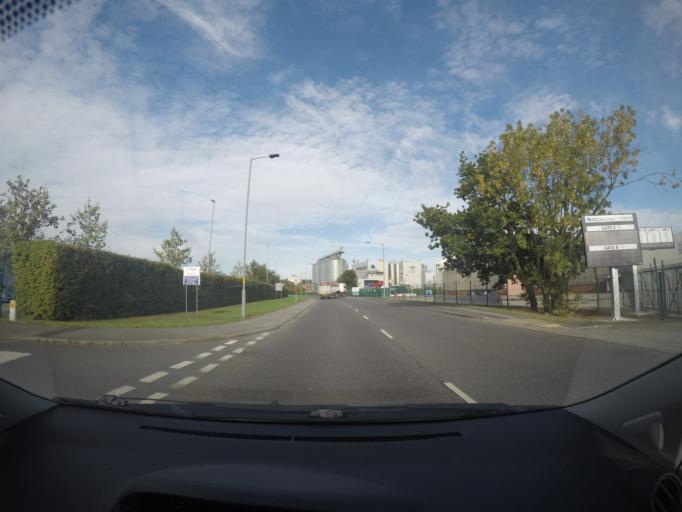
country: GB
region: England
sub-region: North Yorkshire
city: Barlby
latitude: 53.7772
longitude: -1.0436
